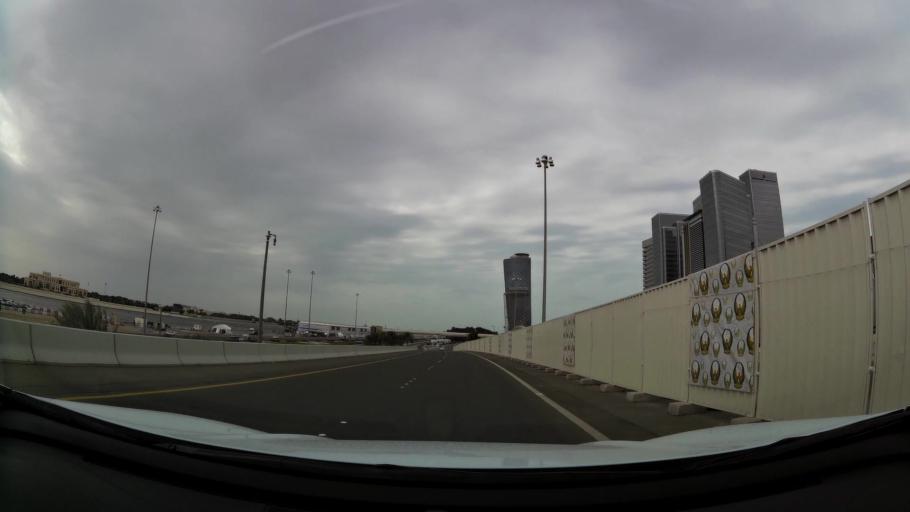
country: AE
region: Abu Dhabi
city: Abu Dhabi
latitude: 24.4160
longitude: 54.4426
